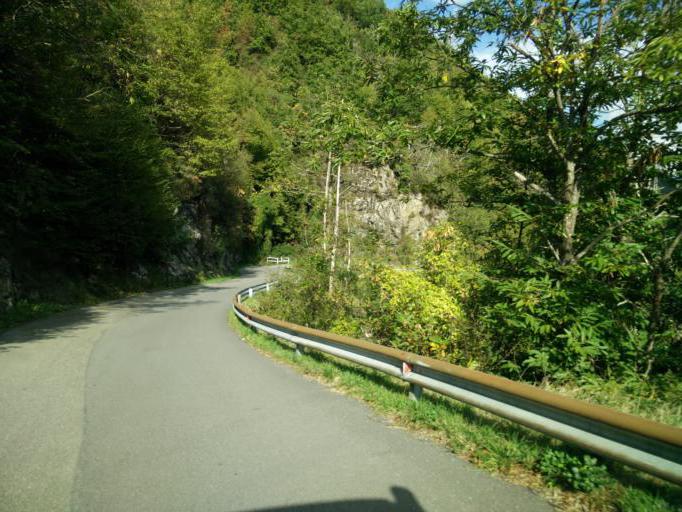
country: IT
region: Tuscany
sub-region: Provincia di Massa-Carrara
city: Zeri
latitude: 44.3496
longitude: 9.7846
